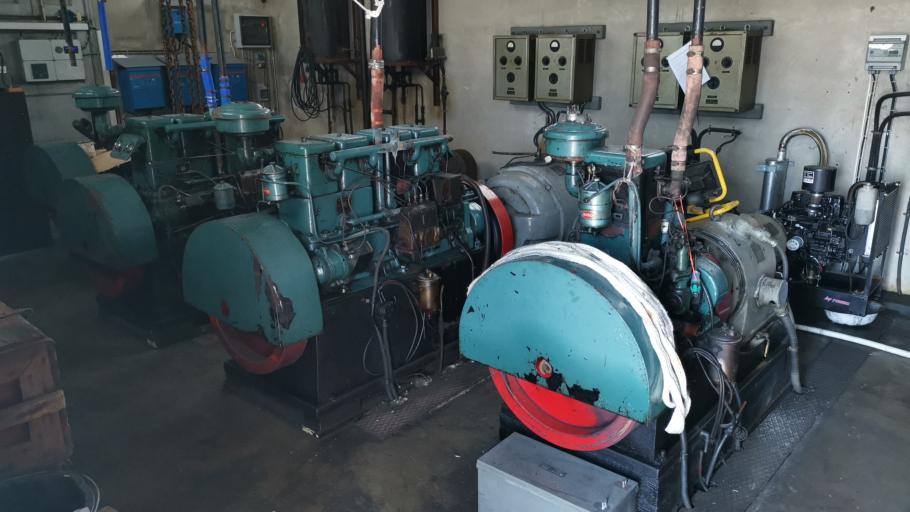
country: AX
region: Alands landsbygd
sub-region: Eckeroe
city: Eckeroe
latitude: 60.3009
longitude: 19.1314
